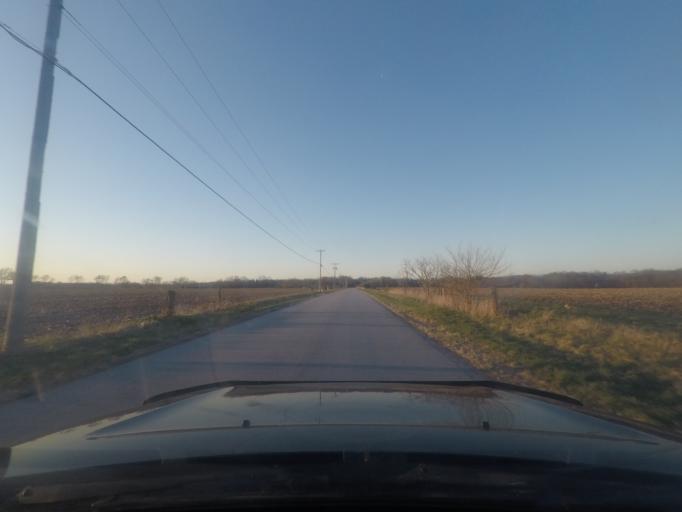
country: US
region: Indiana
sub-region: LaPorte County
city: Kingsford Heights
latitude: 41.5078
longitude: -86.6977
